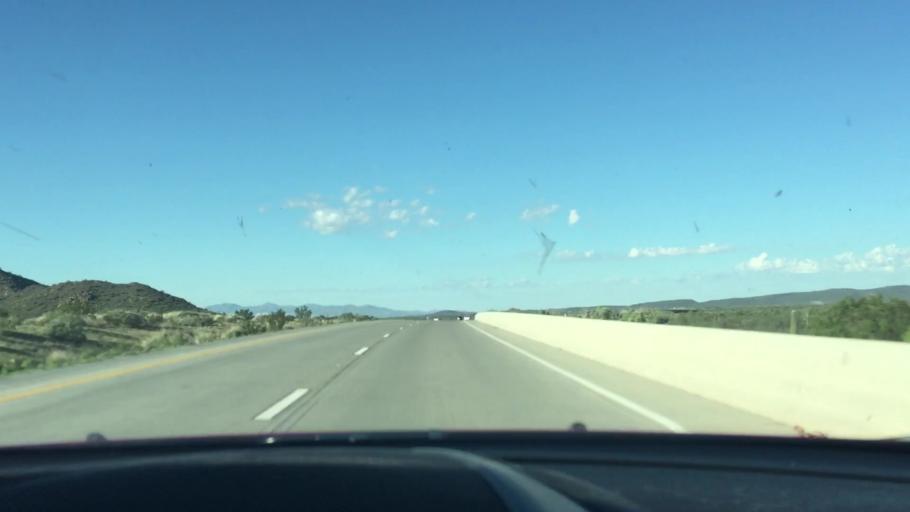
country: US
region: Arizona
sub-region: Maricopa County
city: Anthem
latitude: 33.7815
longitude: -112.2067
